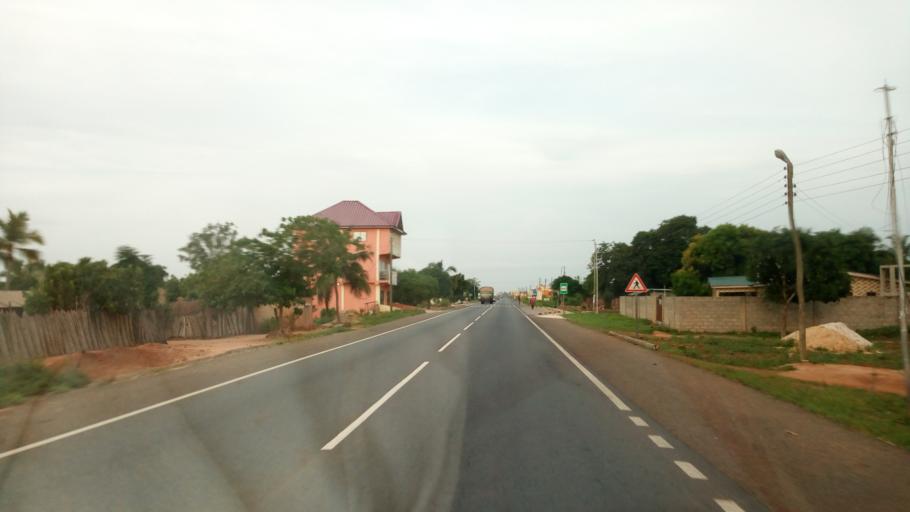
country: TG
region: Maritime
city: Lome
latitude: 6.1130
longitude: 1.1251
